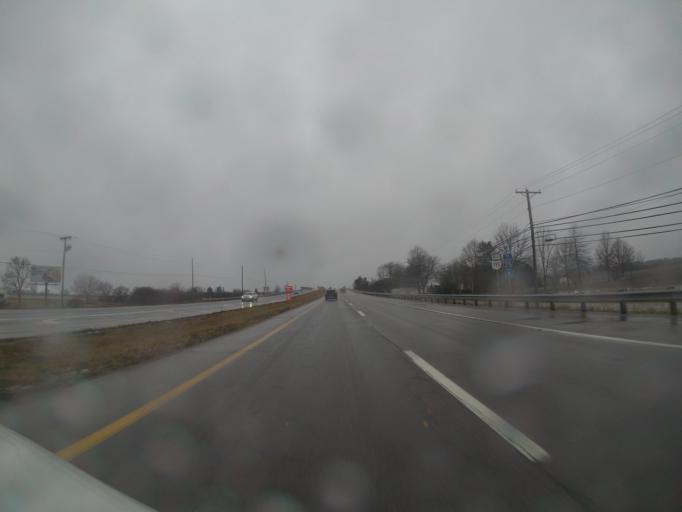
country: US
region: Ohio
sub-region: Wood County
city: Rossford
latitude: 41.5649
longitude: -83.5680
